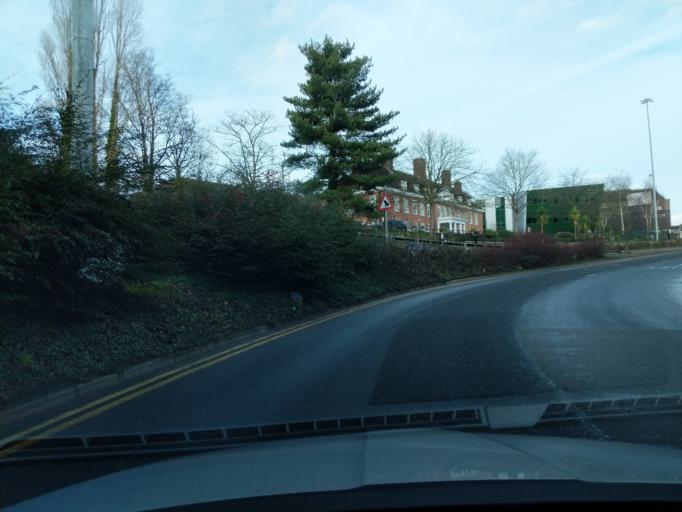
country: GB
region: England
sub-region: Hertfordshire
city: Watford
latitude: 51.6581
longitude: -0.4048
